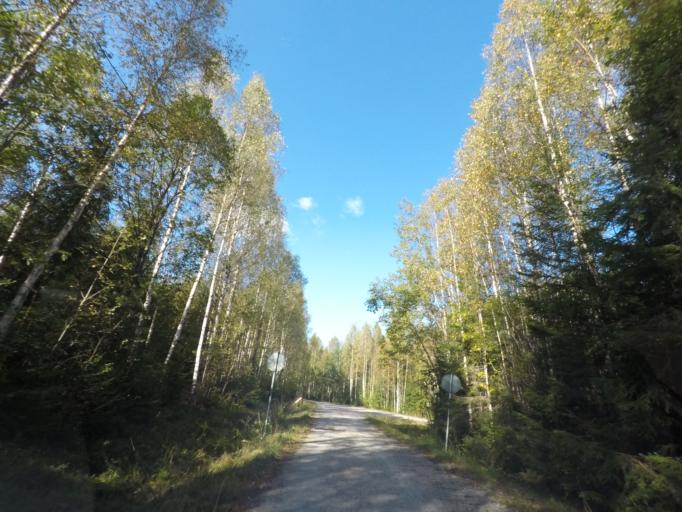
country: SE
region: Vaestmanland
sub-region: Skinnskattebergs Kommun
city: Skinnskatteberg
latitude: 59.8290
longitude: 15.5288
